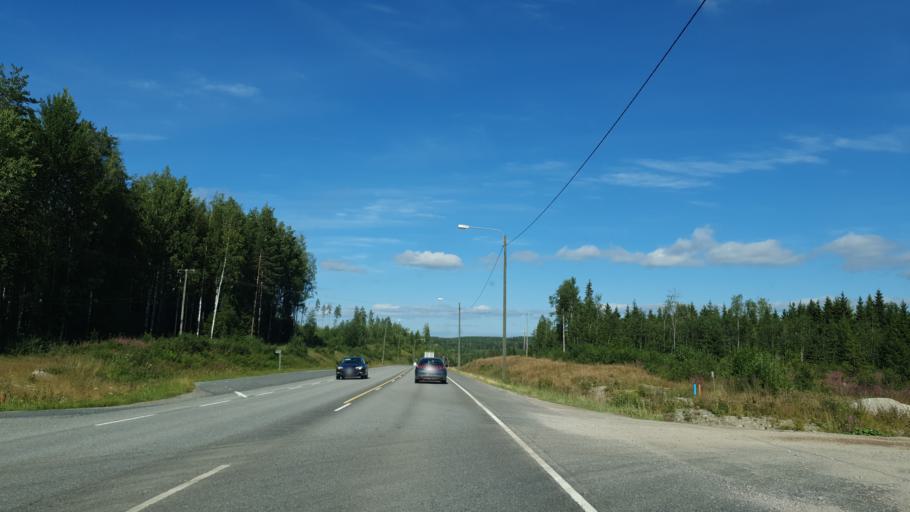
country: FI
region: Central Finland
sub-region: Jyvaeskylae
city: Toivakka
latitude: 62.2491
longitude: 26.0577
